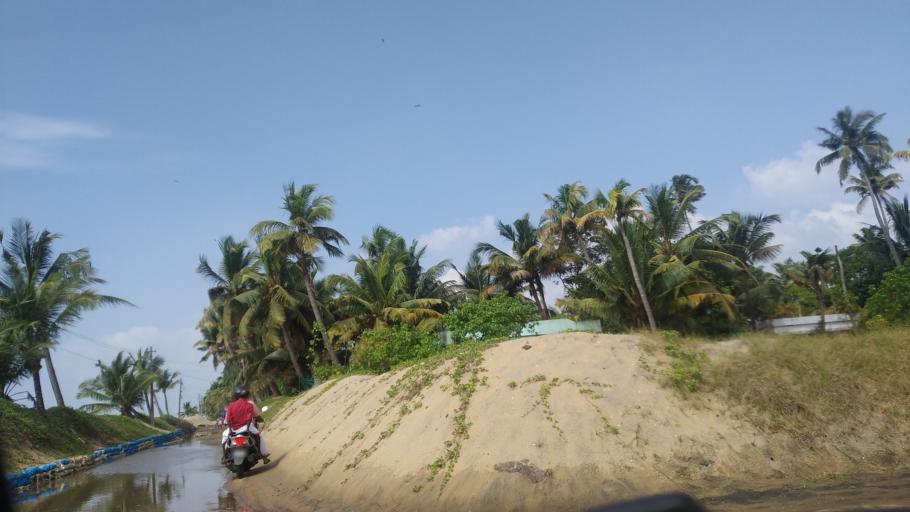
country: IN
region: Kerala
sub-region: Ernakulam
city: Elur
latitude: 10.0727
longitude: 76.1969
